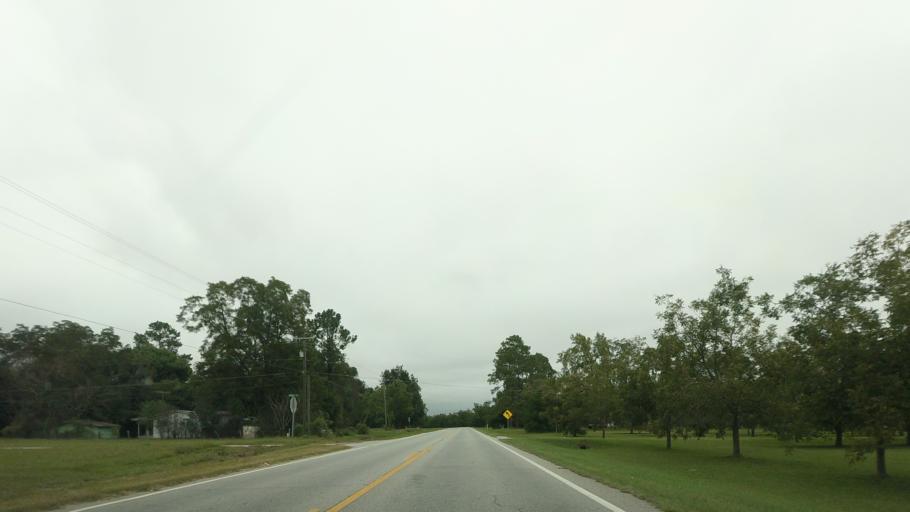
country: US
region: Georgia
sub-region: Berrien County
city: Ray City
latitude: 31.0868
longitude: -83.2057
